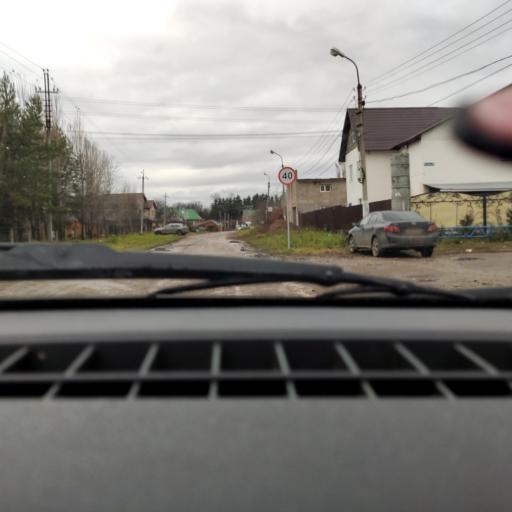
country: RU
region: Bashkortostan
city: Ufa
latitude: 54.7908
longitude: 55.9471
